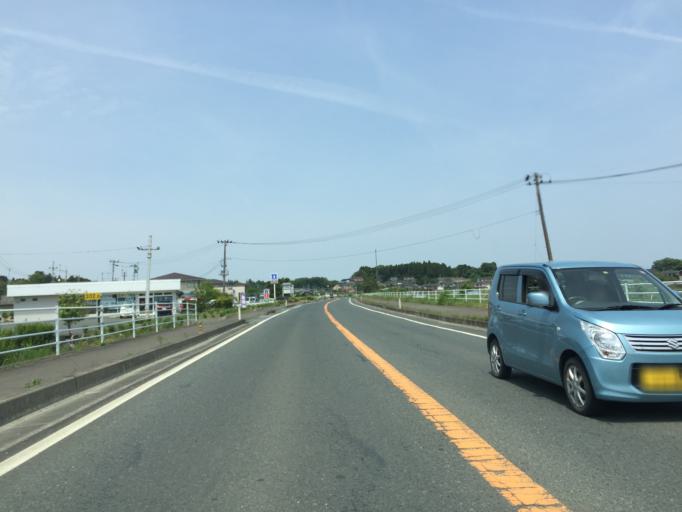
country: JP
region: Miyagi
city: Marumori
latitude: 37.8440
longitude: 140.9190
